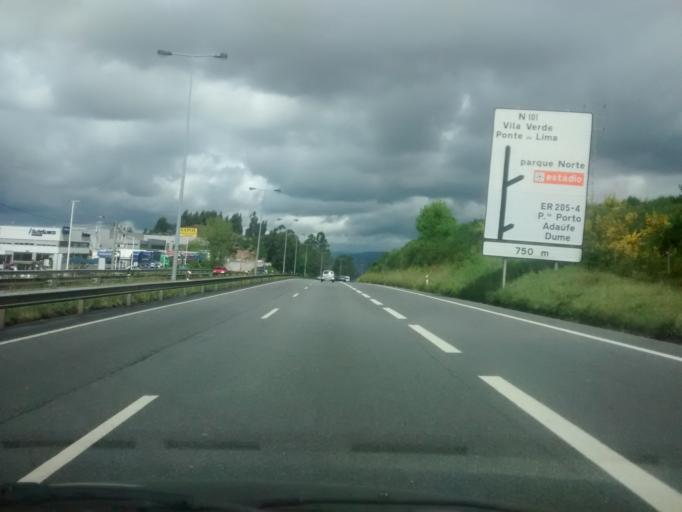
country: PT
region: Braga
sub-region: Braga
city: Braga
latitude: 41.5655
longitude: -8.4195
